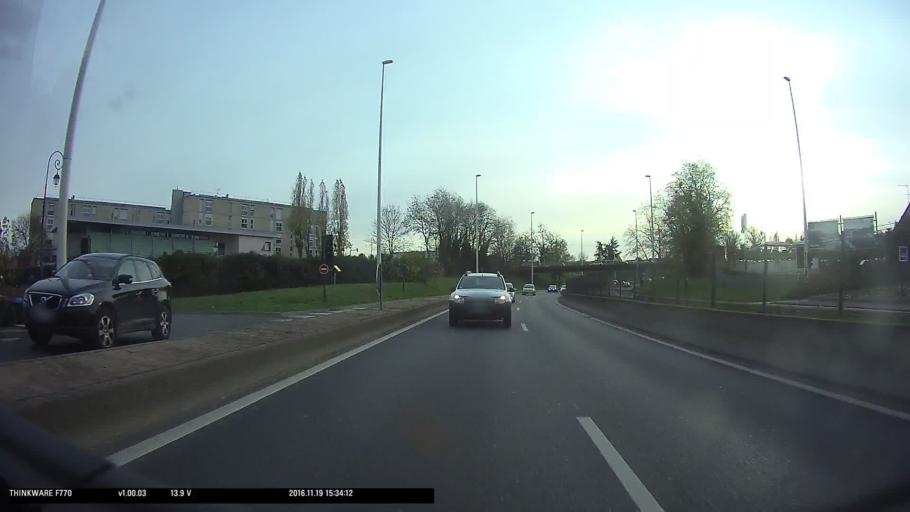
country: FR
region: Ile-de-France
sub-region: Departement du Val-d'Oise
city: Cergy-Pontoise
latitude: 49.0487
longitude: 2.0816
